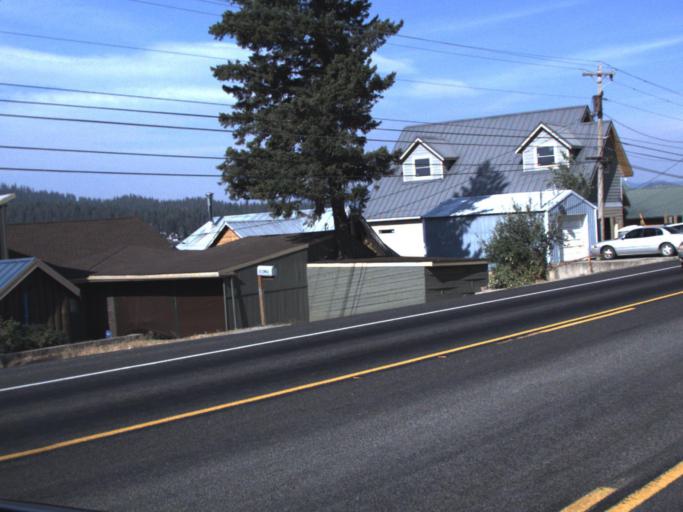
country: US
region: Washington
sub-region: Pend Oreille County
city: Newport
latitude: 48.1204
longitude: -117.2048
